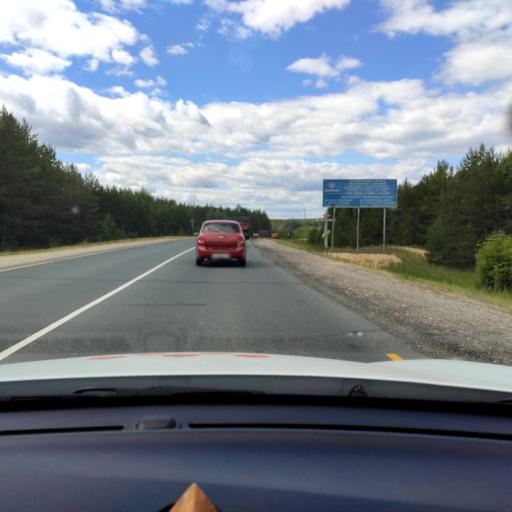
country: RU
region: Mariy-El
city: Volzhsk
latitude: 55.8925
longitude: 48.3999
